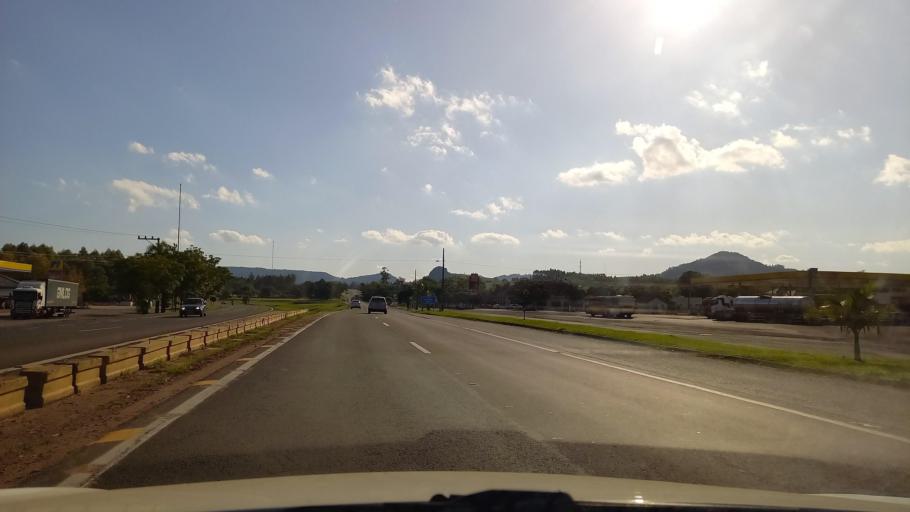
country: BR
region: Rio Grande do Sul
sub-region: Taquari
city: Taquari
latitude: -29.6921
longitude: -51.7066
